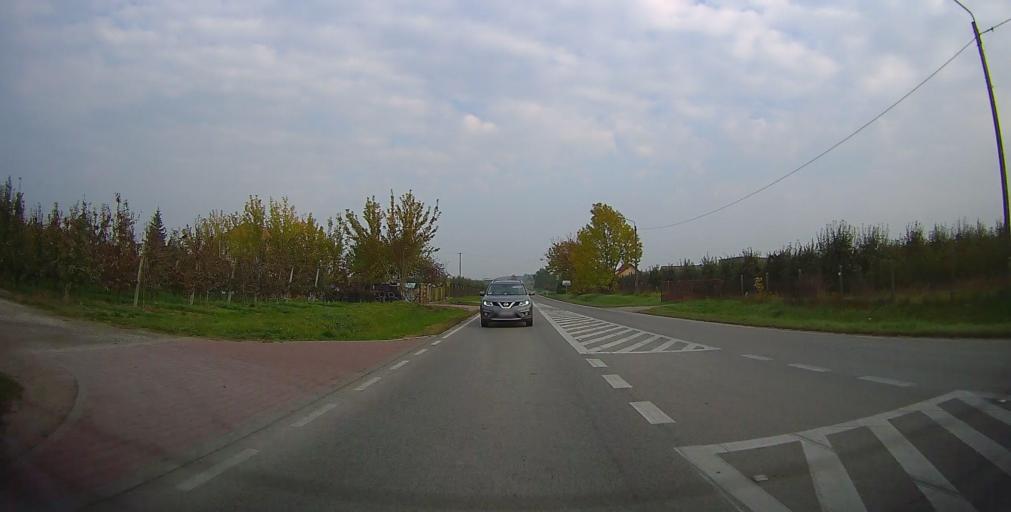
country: PL
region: Masovian Voivodeship
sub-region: Powiat grojecki
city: Belsk Duzy
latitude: 51.7779
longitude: 20.7715
